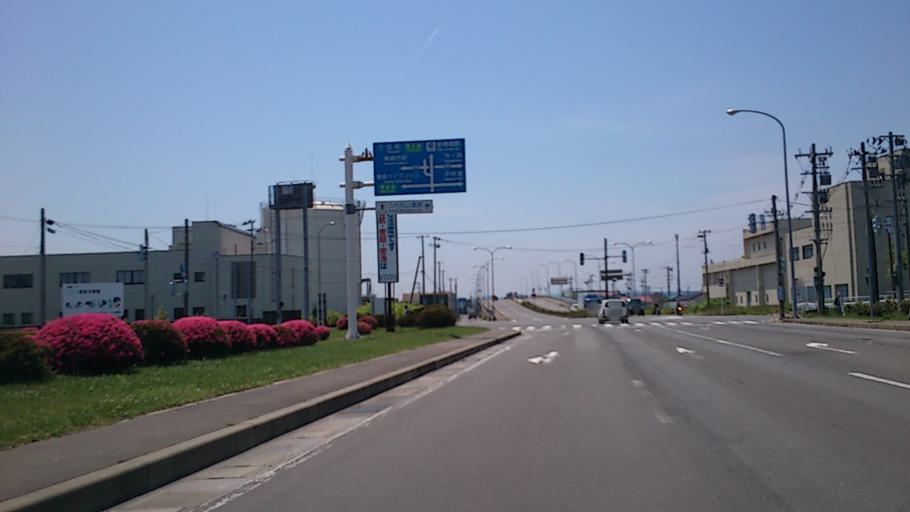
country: JP
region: Aomori
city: Aomori Shi
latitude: 40.8448
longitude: 140.7151
